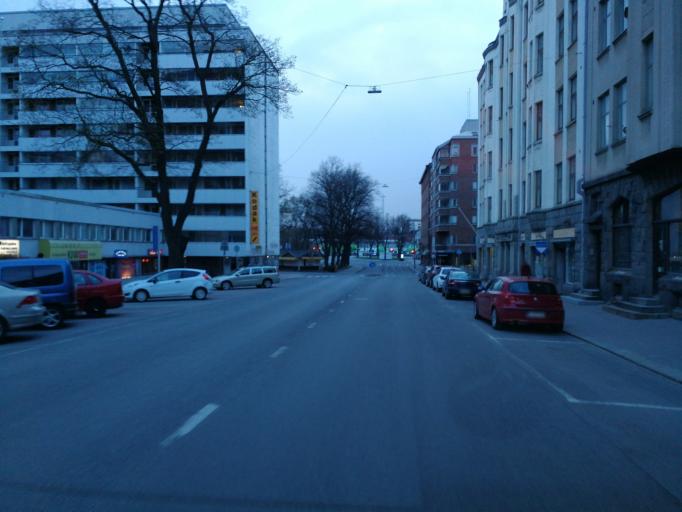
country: FI
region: Varsinais-Suomi
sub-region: Turku
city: Turku
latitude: 60.4528
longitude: 22.2562
